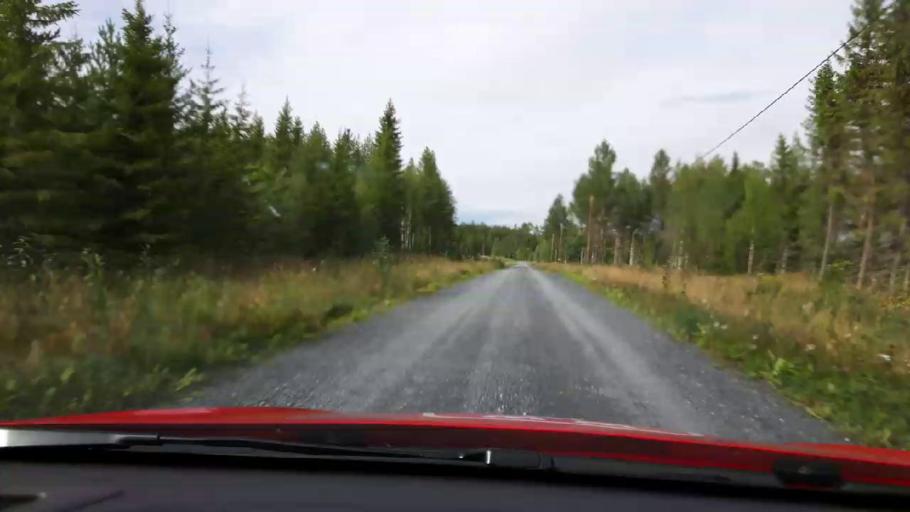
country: SE
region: Jaemtland
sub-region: Are Kommun
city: Jarpen
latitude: 63.2721
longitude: 13.7528
